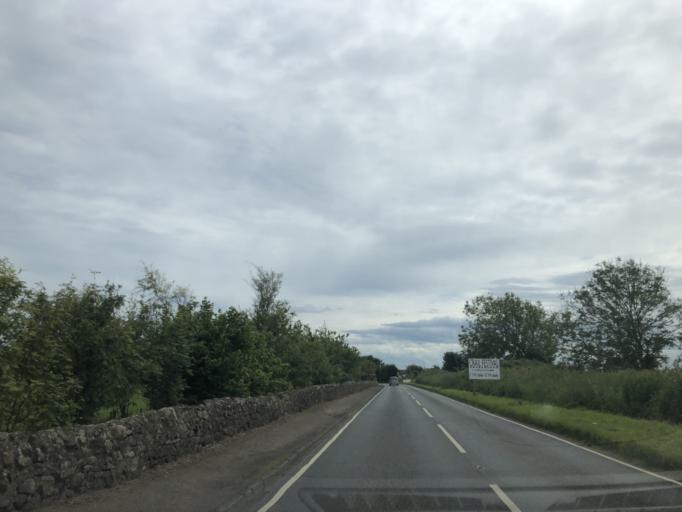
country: GB
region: Scotland
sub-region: Fife
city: Anstruther
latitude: 56.2646
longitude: -2.6340
